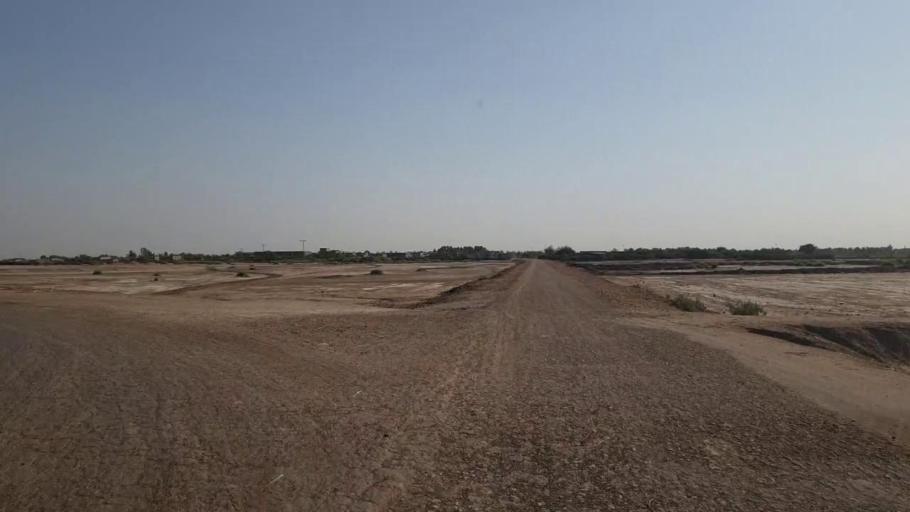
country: PK
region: Sindh
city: Matli
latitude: 25.0423
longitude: 68.7231
